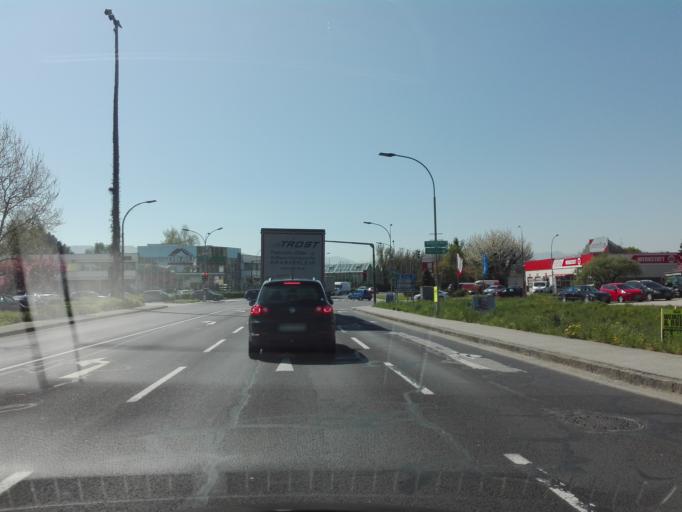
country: AT
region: Upper Austria
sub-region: Steyr Stadt
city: Steyr
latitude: 48.0483
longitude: 14.4140
